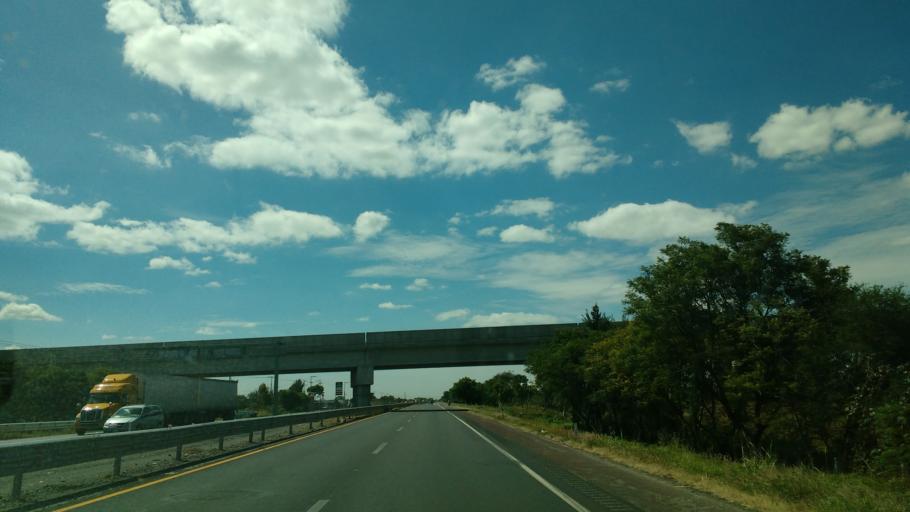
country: MX
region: Guanajuato
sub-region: Apaseo el Grande
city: La Labor
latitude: 20.5362
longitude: -100.7067
